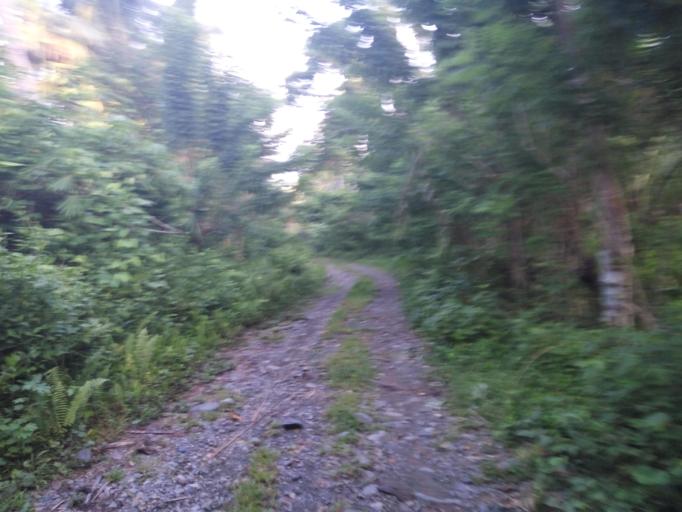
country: PH
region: Central Luzon
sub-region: Province of Aurora
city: Maria Aurora
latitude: 15.8888
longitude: 121.5474
